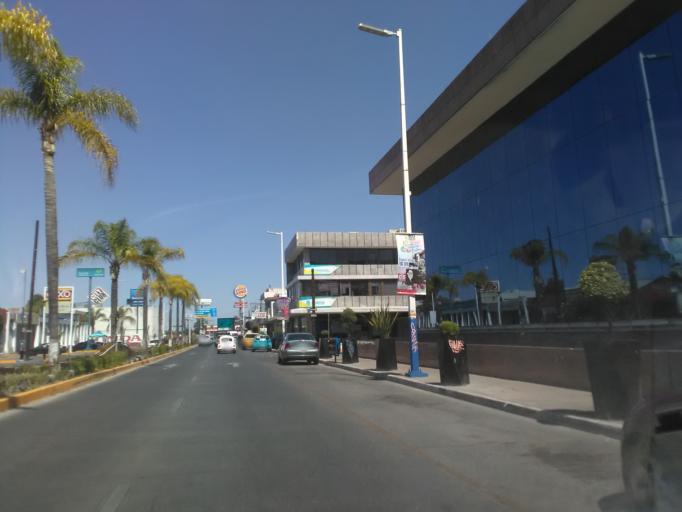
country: MX
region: Durango
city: Victoria de Durango
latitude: 24.0289
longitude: -104.6452
